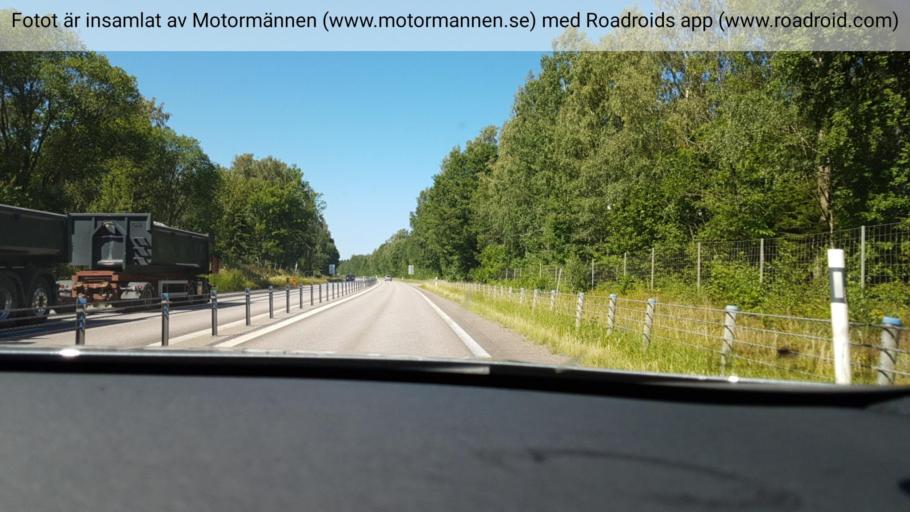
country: SE
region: Vaestra Goetaland
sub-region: Skovde Kommun
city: Stopen
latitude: 58.4893
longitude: 13.8508
